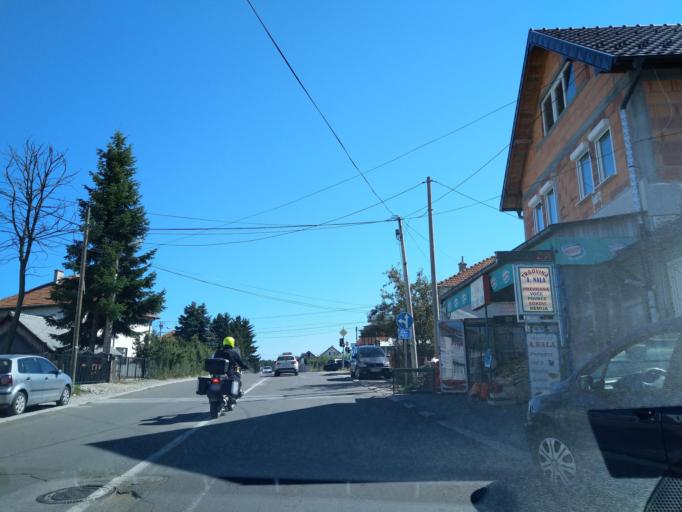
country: RS
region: Central Serbia
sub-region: Zlatiborski Okrug
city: Sjenica
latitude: 43.2735
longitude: 20.0092
